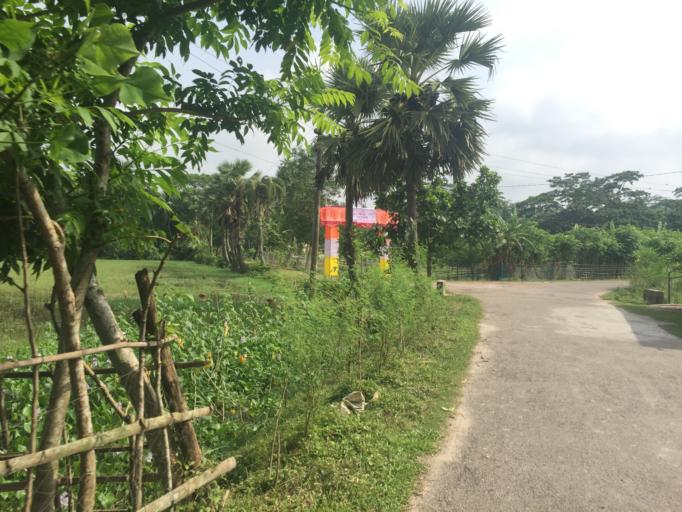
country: BD
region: Barisal
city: Mathba
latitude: 22.2489
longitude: 89.9139
